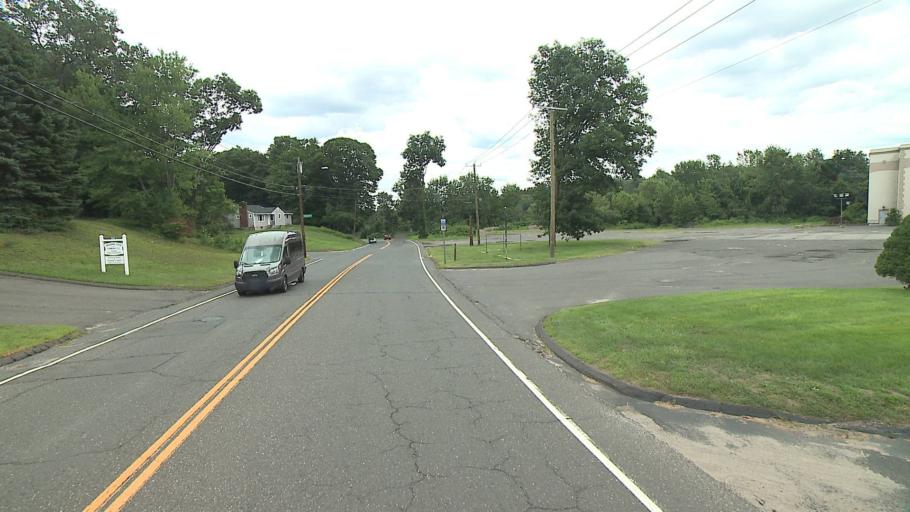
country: US
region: Connecticut
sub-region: New Haven County
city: Waterbury
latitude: 41.5437
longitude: -73.0775
